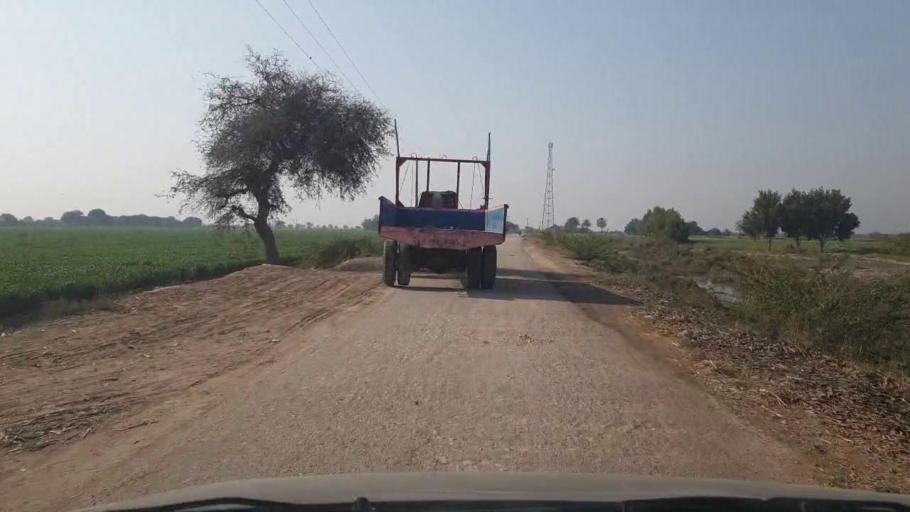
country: PK
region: Sindh
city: Mirwah Gorchani
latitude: 25.2990
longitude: 69.1476
